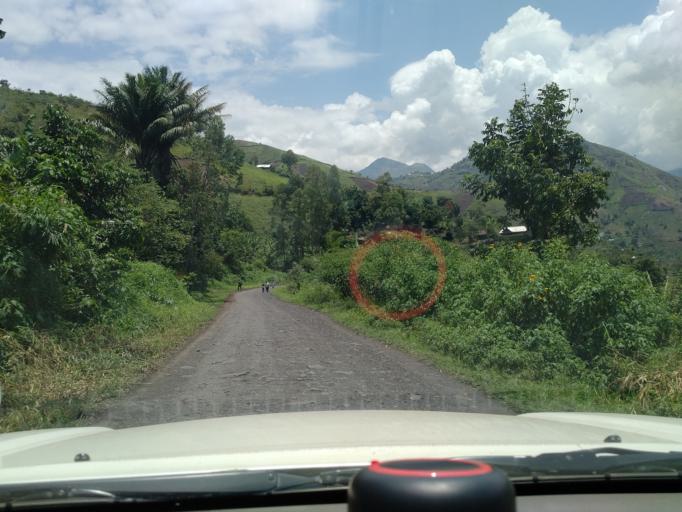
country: CD
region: Nord Kivu
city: Sake
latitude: -1.7416
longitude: 28.9965
